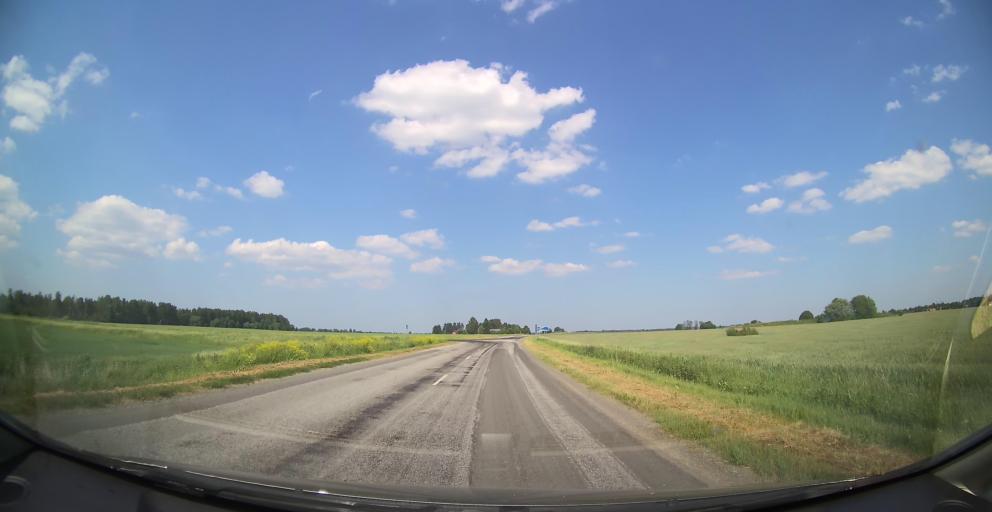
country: EE
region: Harju
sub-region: Raasiku vald
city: Arukula
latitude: 59.4244
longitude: 25.0784
